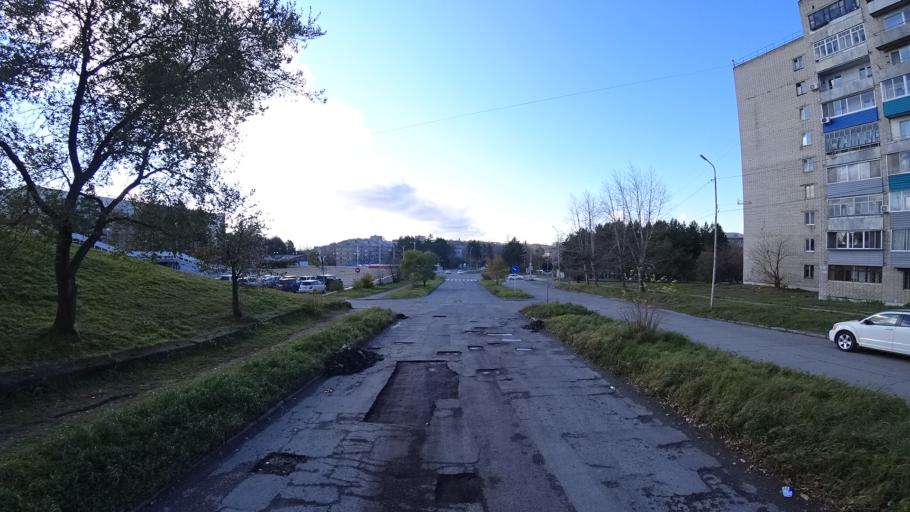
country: RU
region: Khabarovsk Krai
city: Amursk
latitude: 50.2279
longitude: 136.9108
